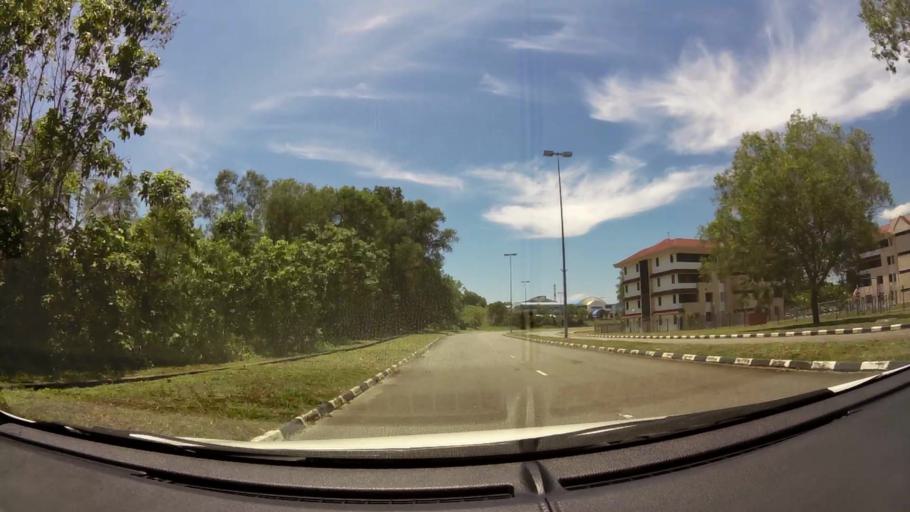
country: BN
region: Brunei and Muara
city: Bandar Seri Begawan
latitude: 4.9313
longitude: 114.9501
